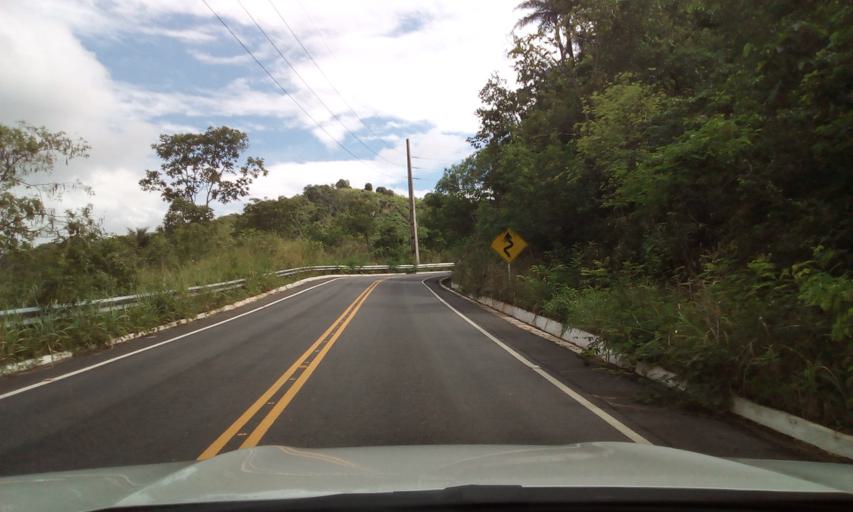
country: BR
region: Paraiba
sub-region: Alagoinha
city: Alagoinha
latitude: -6.8872
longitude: -35.5811
